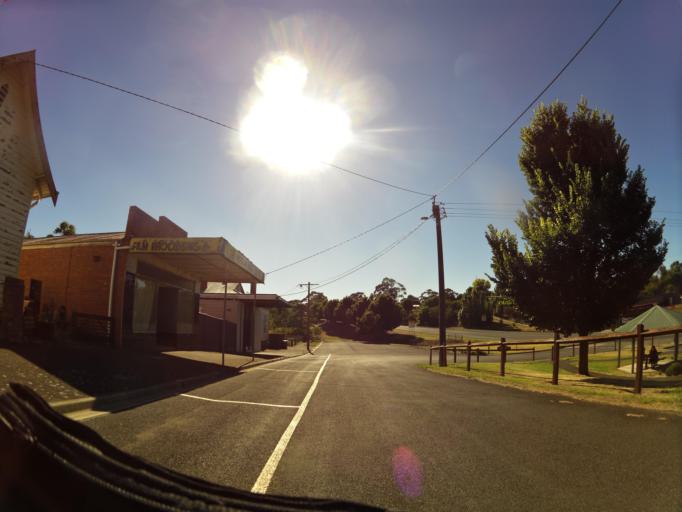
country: AU
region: Victoria
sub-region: Ballarat North
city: Delacombe
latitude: -37.6857
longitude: 143.3659
